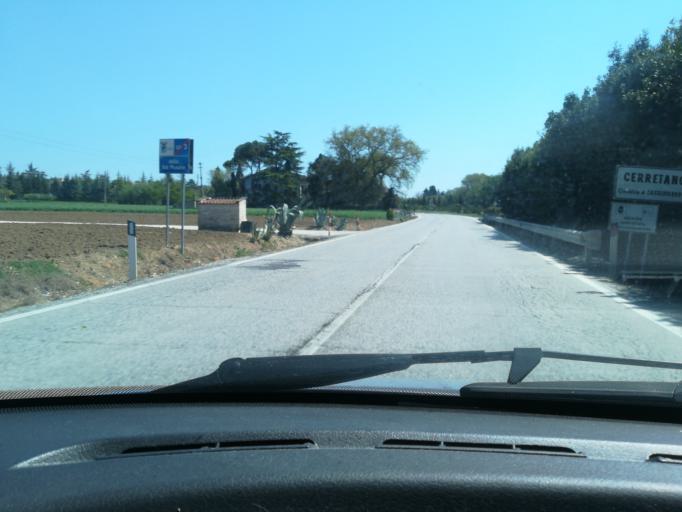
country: IT
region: The Marches
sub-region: Provincia di Ancona
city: Castelfidardo
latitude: 43.4525
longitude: 13.5292
